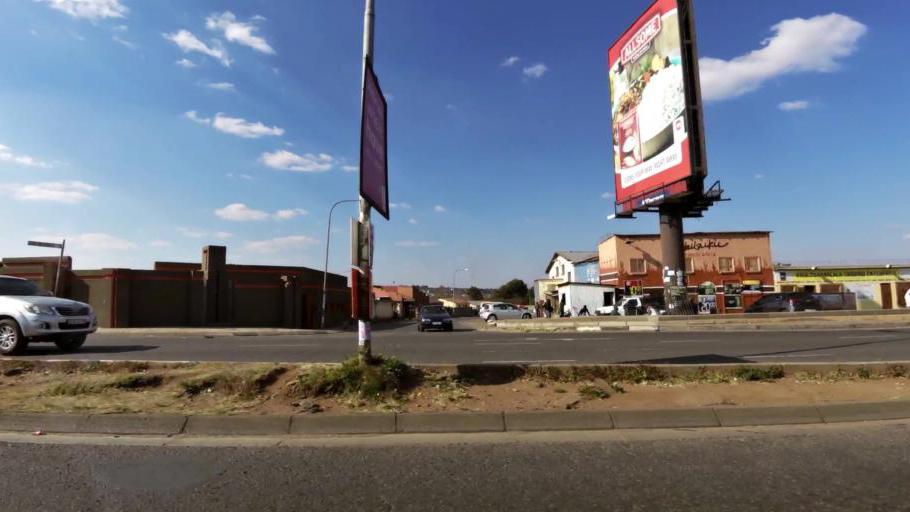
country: ZA
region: Gauteng
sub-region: City of Johannesburg Metropolitan Municipality
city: Soweto
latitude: -26.2216
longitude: 27.8721
